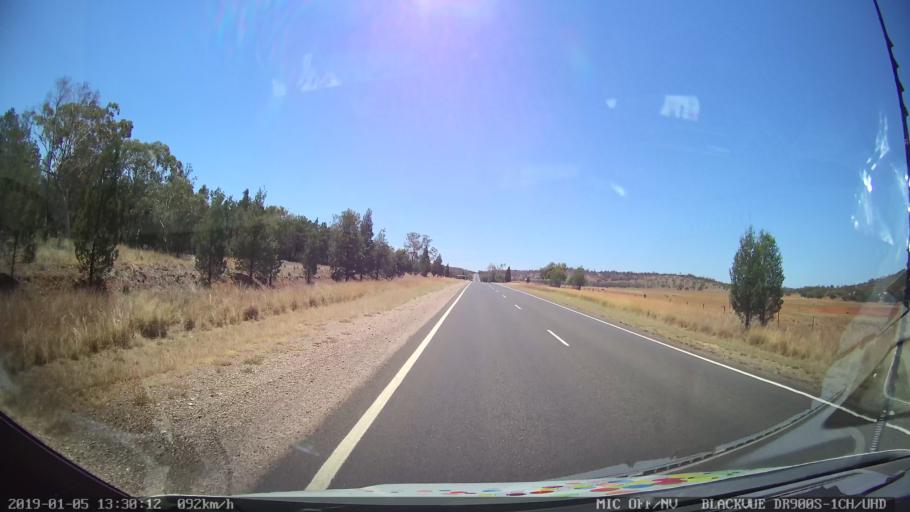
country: AU
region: New South Wales
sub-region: Gunnedah
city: Gunnedah
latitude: -31.0210
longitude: 150.0673
